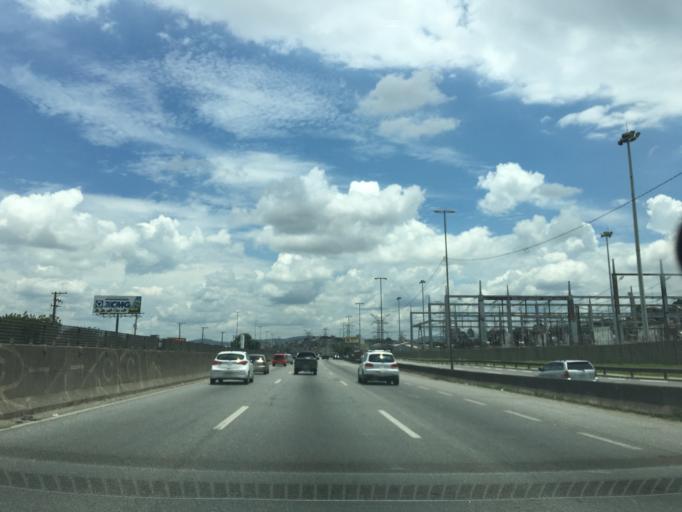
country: BR
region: Sao Paulo
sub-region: Guarulhos
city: Guarulhos
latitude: -23.4845
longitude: -46.5597
